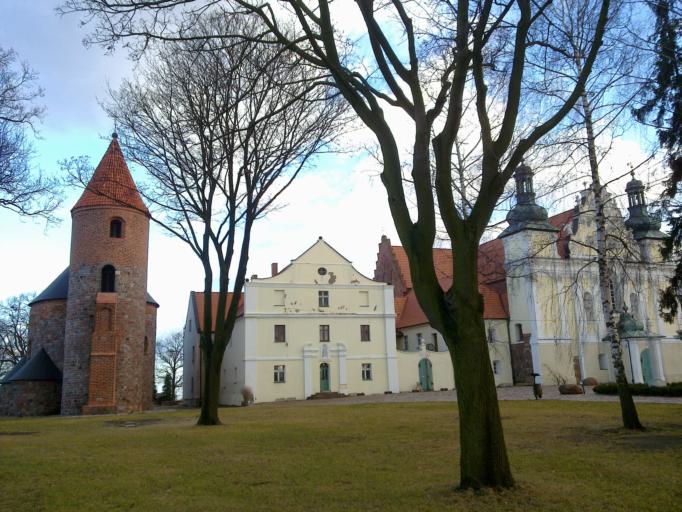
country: PL
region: Kujawsko-Pomorskie
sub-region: Powiat mogilenski
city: Strzelno
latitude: 52.6301
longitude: 18.1783
